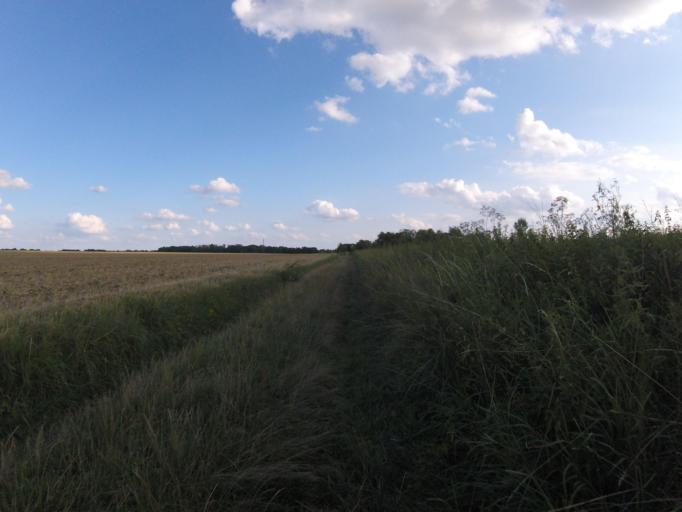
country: DE
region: Brandenburg
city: Mittenwalde
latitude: 52.3009
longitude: 13.5445
